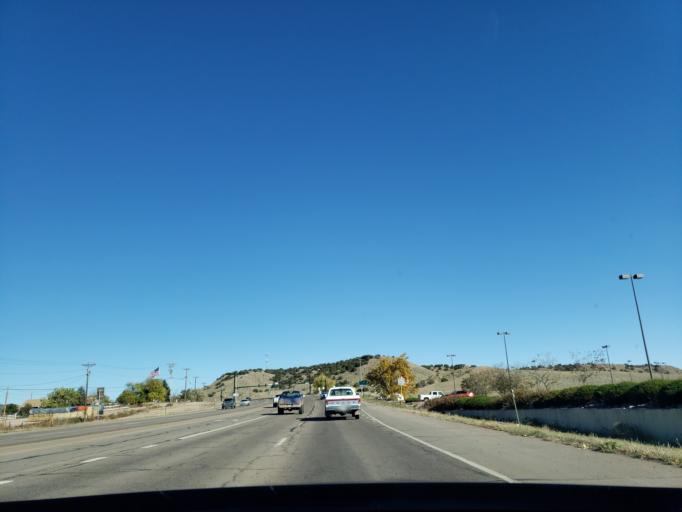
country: US
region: Colorado
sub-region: Fremont County
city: Lincoln Park
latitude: 38.4470
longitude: -105.1806
